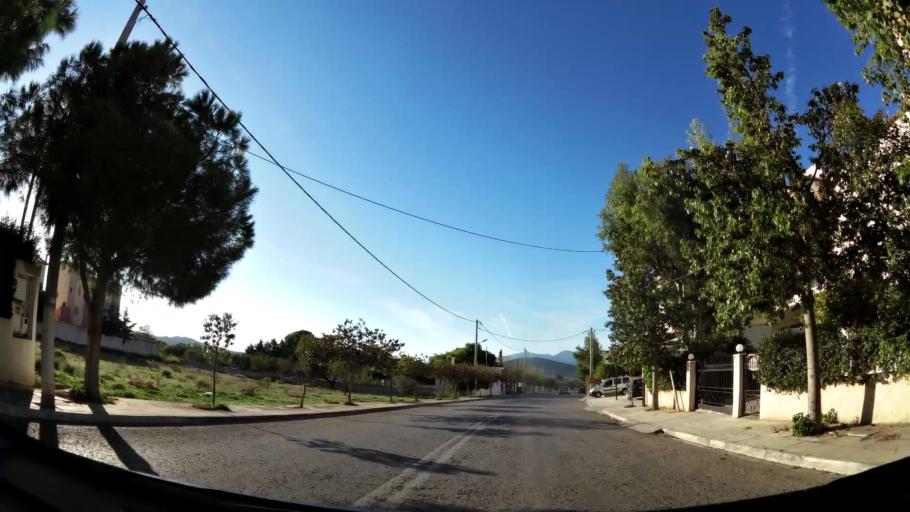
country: GR
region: Attica
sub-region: Nomarchia Anatolikis Attikis
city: Kalyvia Thorikou
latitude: 37.8349
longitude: 23.9255
